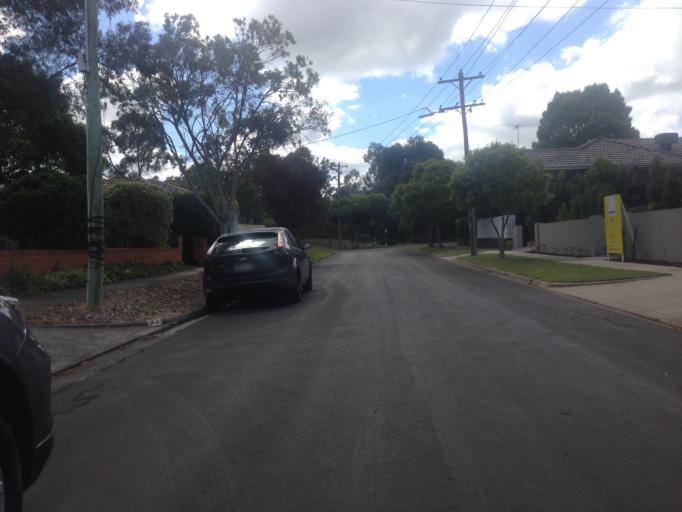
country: AU
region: Victoria
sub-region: Manningham
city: Bulleen
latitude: -37.7812
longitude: 145.0819
